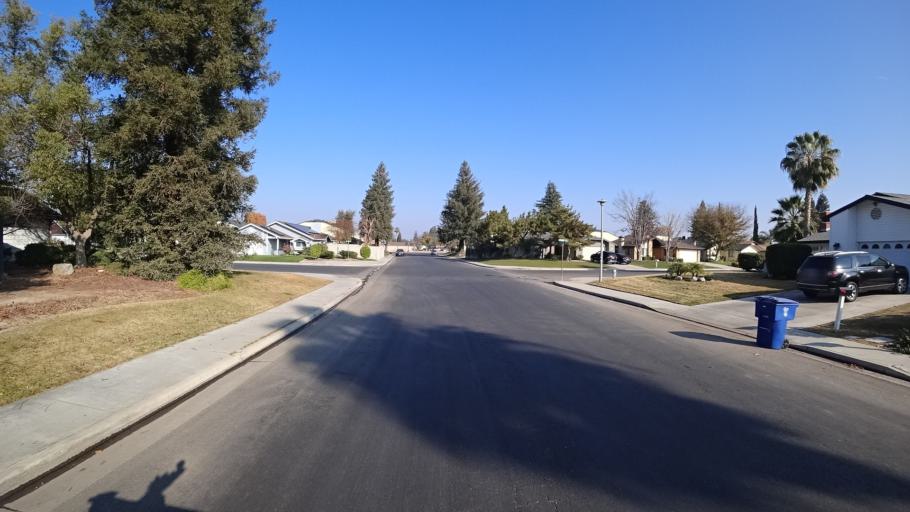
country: US
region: California
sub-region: Kern County
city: Greenacres
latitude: 35.3233
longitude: -119.0873
